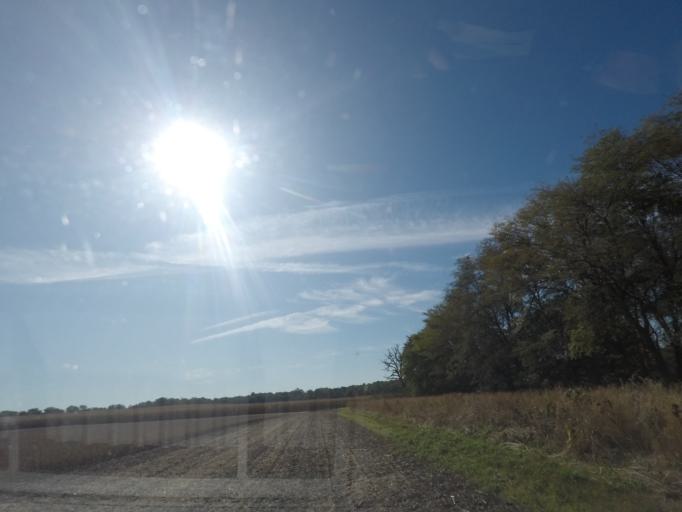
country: US
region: Iowa
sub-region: Story County
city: Nevada
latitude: 42.0308
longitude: -93.3764
